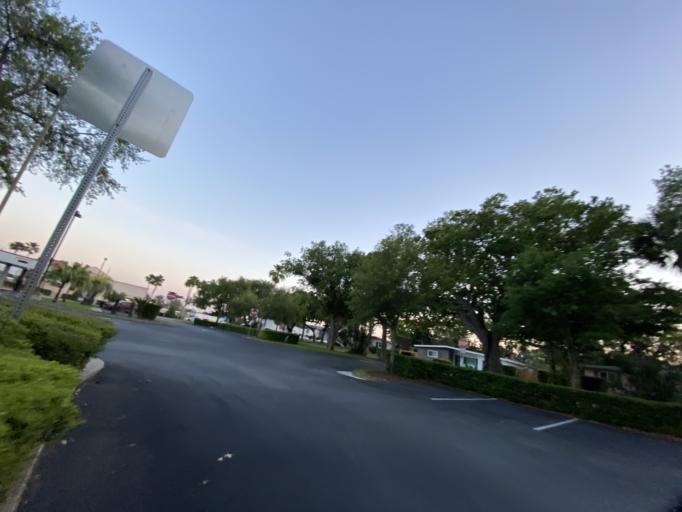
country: US
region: Florida
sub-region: Volusia County
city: South Daytona
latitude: 29.1680
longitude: -81.0007
